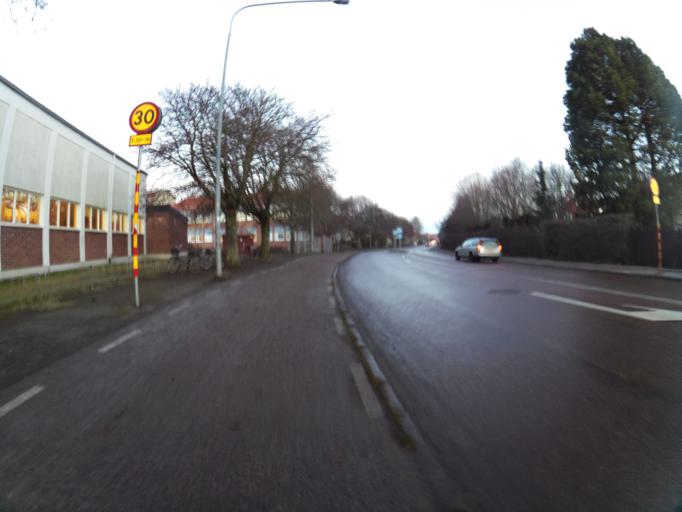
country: SE
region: Gaevleborg
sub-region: Gavle Kommun
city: Gavle
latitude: 60.6681
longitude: 17.1343
